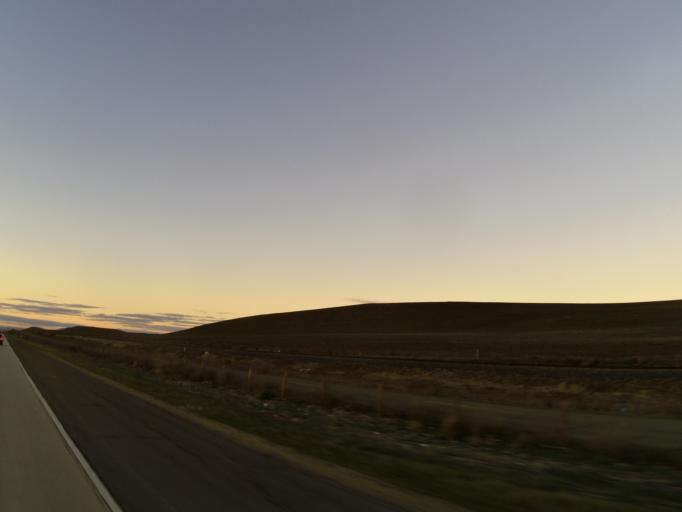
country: US
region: California
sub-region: Monterey County
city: King City
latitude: 36.1351
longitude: -121.0321
